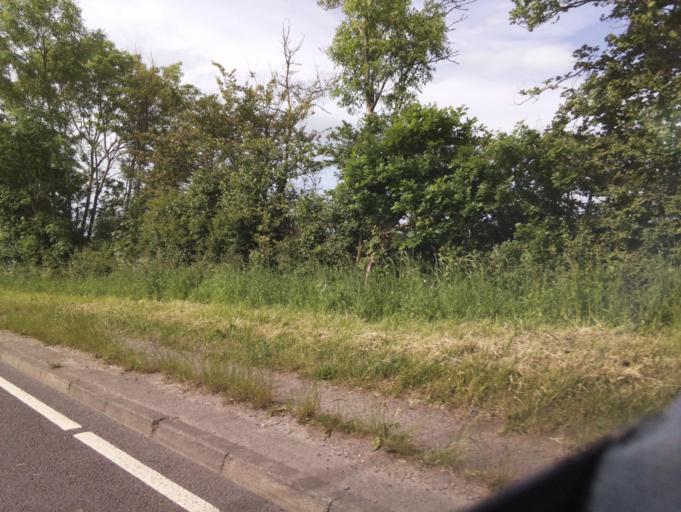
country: GB
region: England
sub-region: Worcestershire
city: Pershore
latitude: 52.1195
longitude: -2.1002
